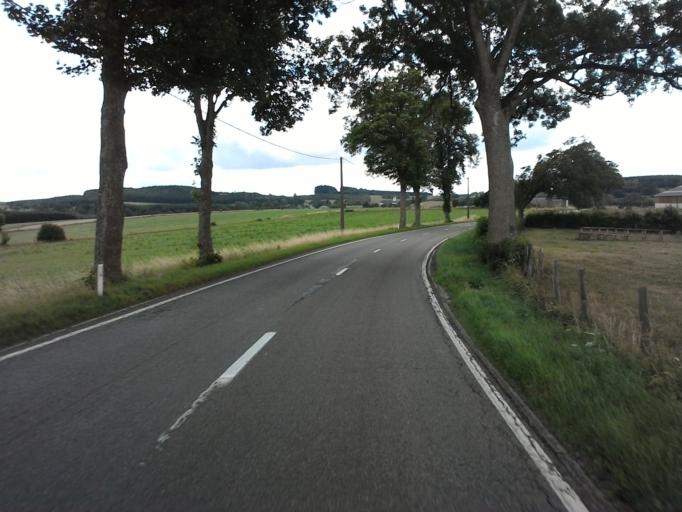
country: BE
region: Wallonia
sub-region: Province du Luxembourg
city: Leglise
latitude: 49.8067
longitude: 5.5259
